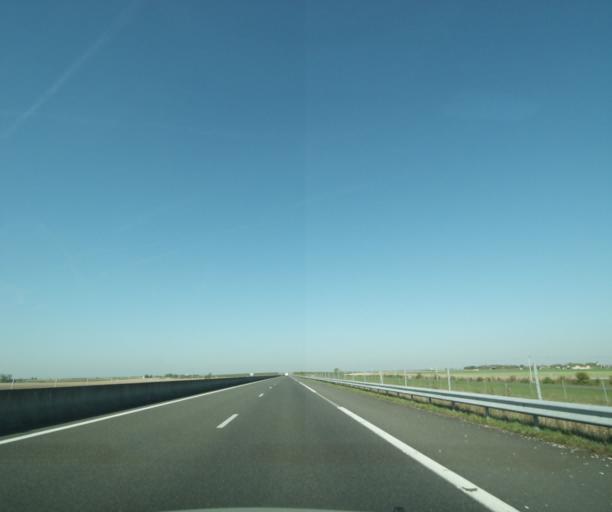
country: FR
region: Centre
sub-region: Departement du Loiret
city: Corbeilles
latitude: 48.0929
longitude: 2.5425
